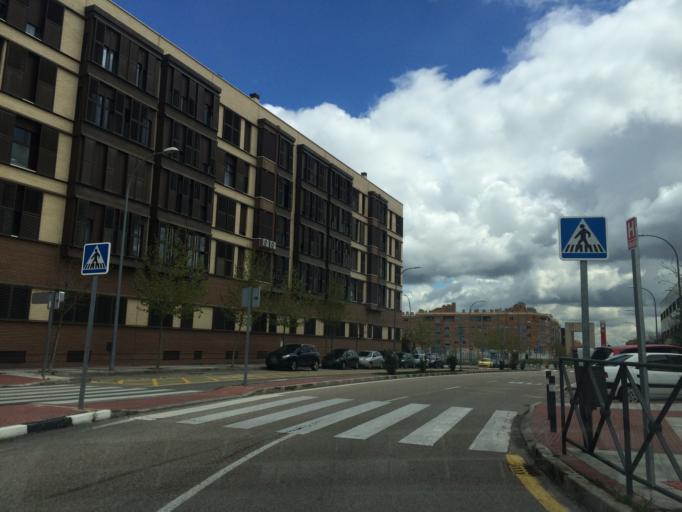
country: ES
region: Madrid
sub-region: Provincia de Madrid
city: Alcobendas
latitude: 40.5504
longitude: -3.6622
